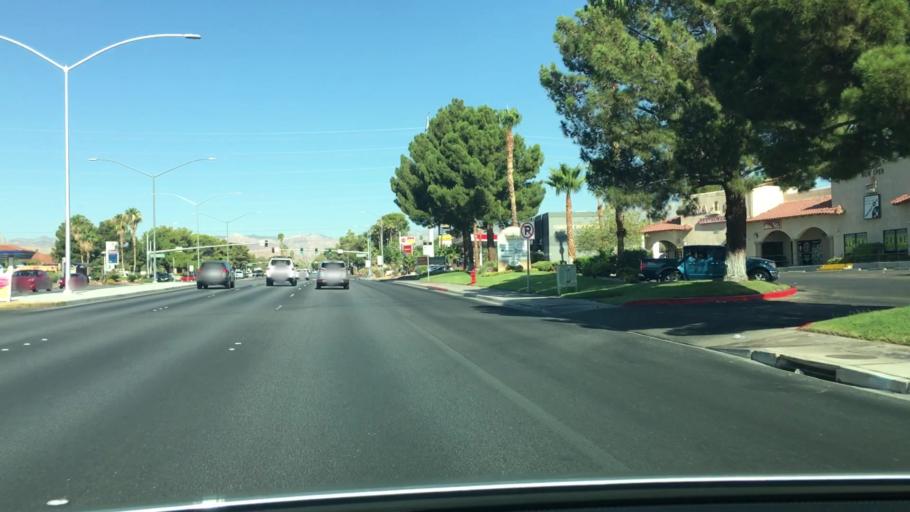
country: US
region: Nevada
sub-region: Clark County
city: Spring Valley
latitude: 36.1441
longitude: -115.2768
